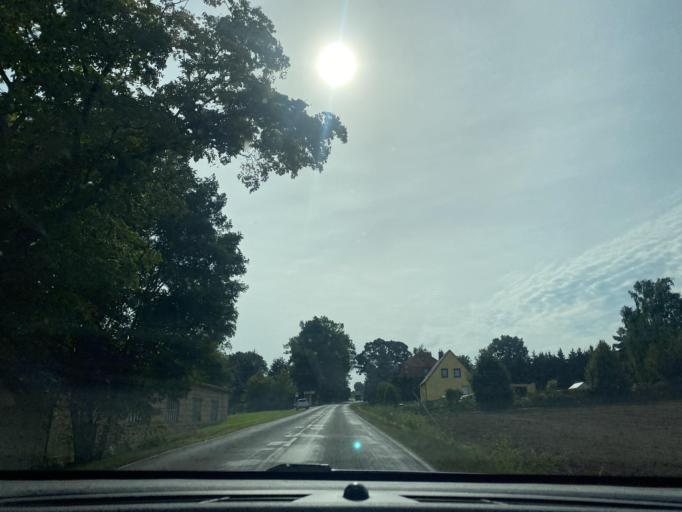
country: DE
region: Saxony
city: Reichenbach
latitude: 51.1612
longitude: 14.7923
